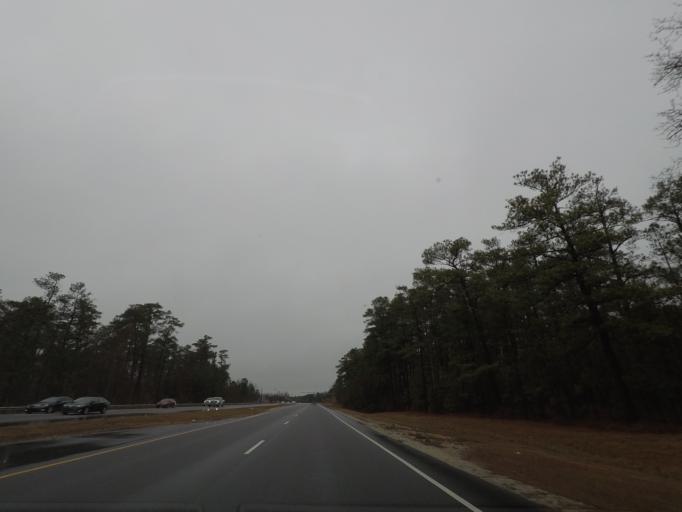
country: US
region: North Carolina
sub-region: Cumberland County
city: Spring Lake
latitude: 35.2411
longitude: -79.0215
